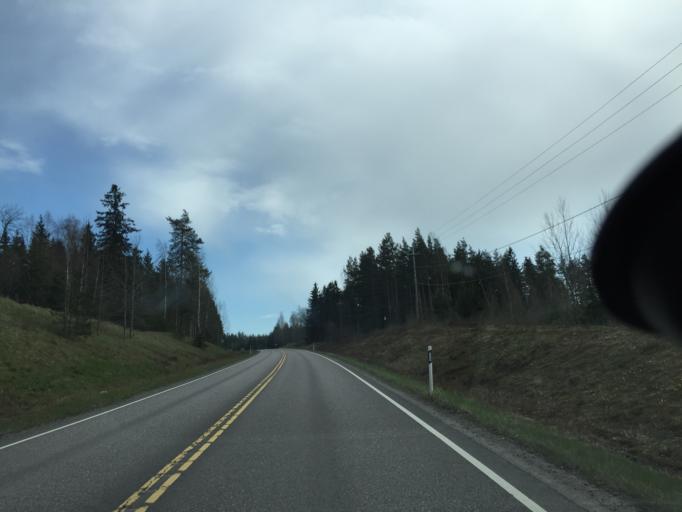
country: FI
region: Uusimaa
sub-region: Raaseporin
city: Ekenaes
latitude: 60.0454
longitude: 23.3345
